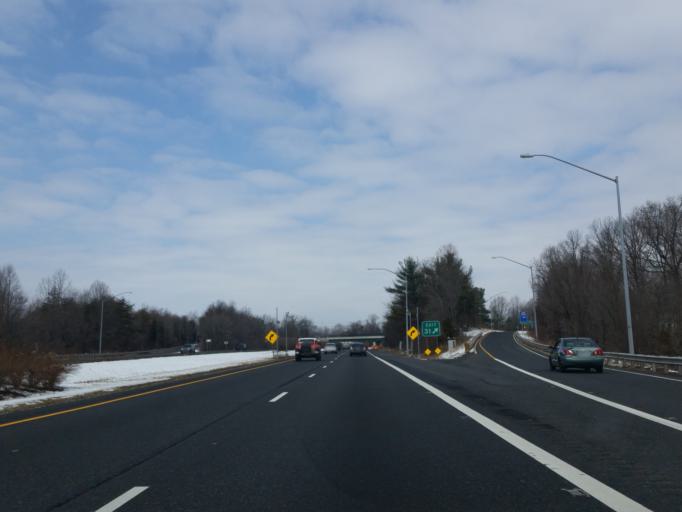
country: US
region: Pennsylvania
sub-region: York County
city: New Freedom
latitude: 39.6291
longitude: -76.6703
